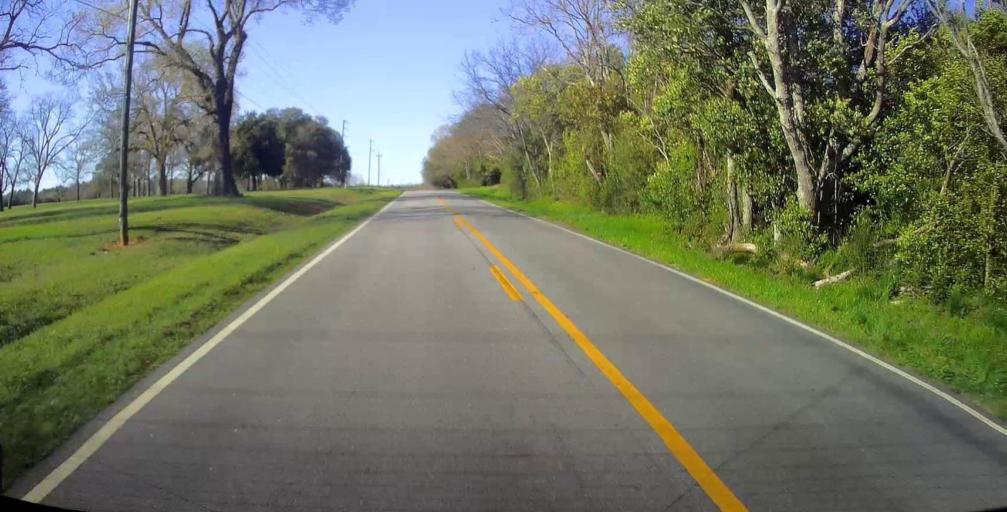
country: US
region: Georgia
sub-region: Houston County
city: Perry
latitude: 32.4377
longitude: -83.7367
